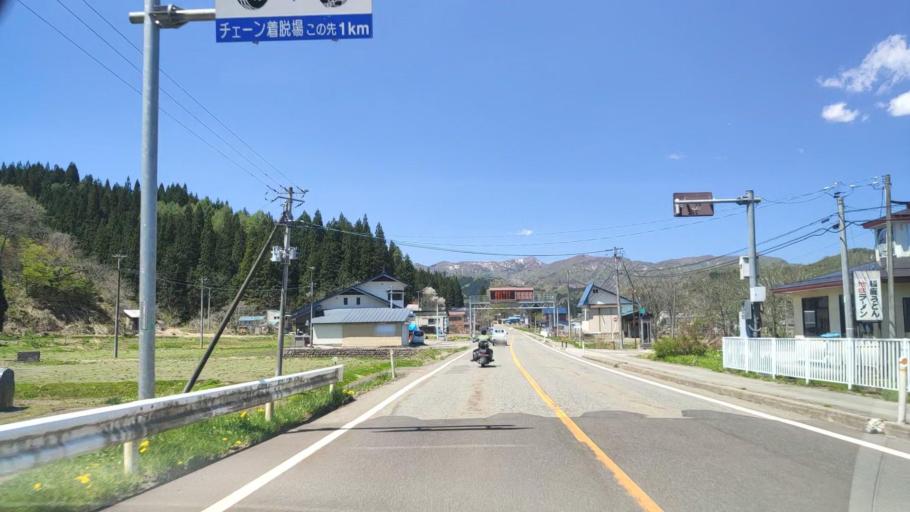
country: JP
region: Akita
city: Yuzawa
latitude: 39.0479
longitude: 140.4164
